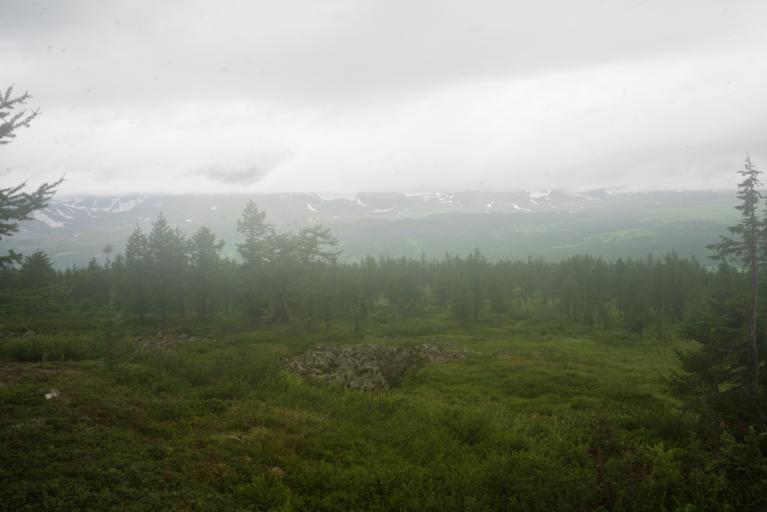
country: RU
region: Komi Republic
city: Synya
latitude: 64.7793
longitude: 59.0285
